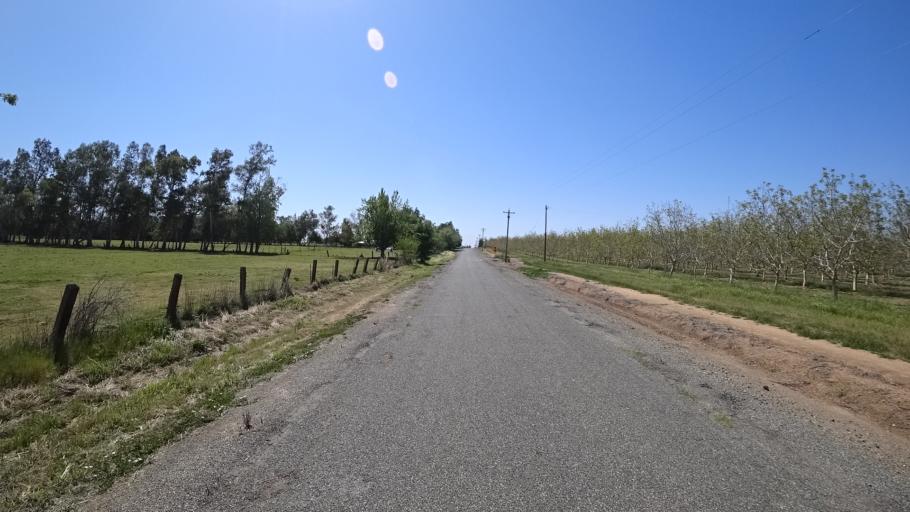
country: US
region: California
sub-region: Glenn County
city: Orland
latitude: 39.7894
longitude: -122.1598
